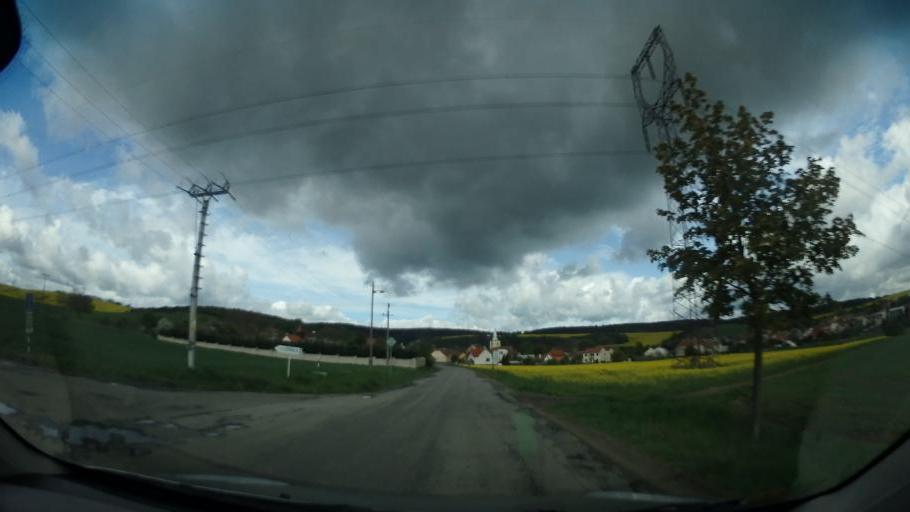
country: CZ
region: South Moravian
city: Ricany
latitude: 49.2325
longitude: 16.4085
